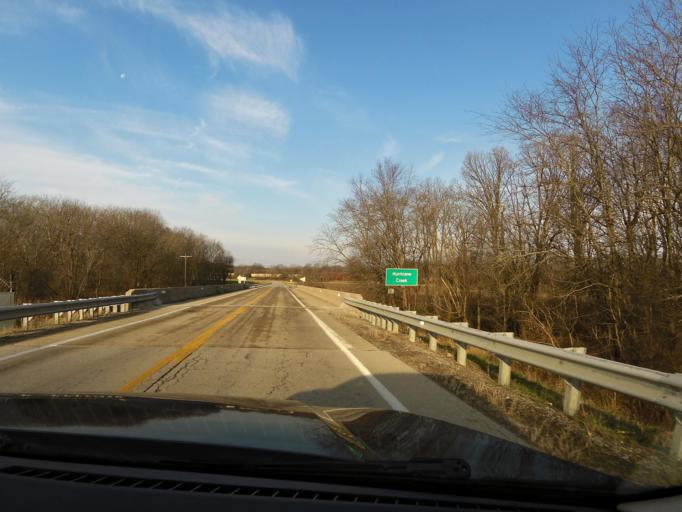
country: US
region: Illinois
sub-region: Fayette County
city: Vandalia
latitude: 38.9221
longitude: -89.2363
